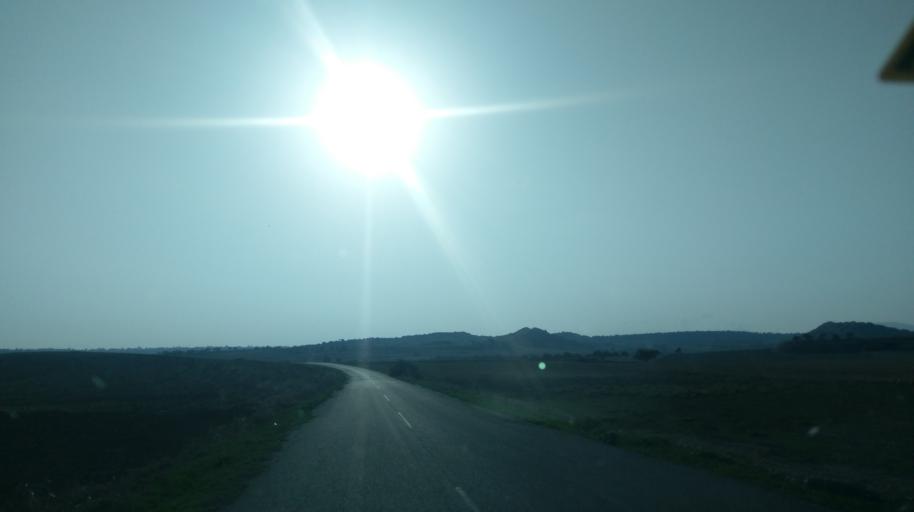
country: CY
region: Ammochostos
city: Leonarisso
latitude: 35.4456
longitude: 34.0907
